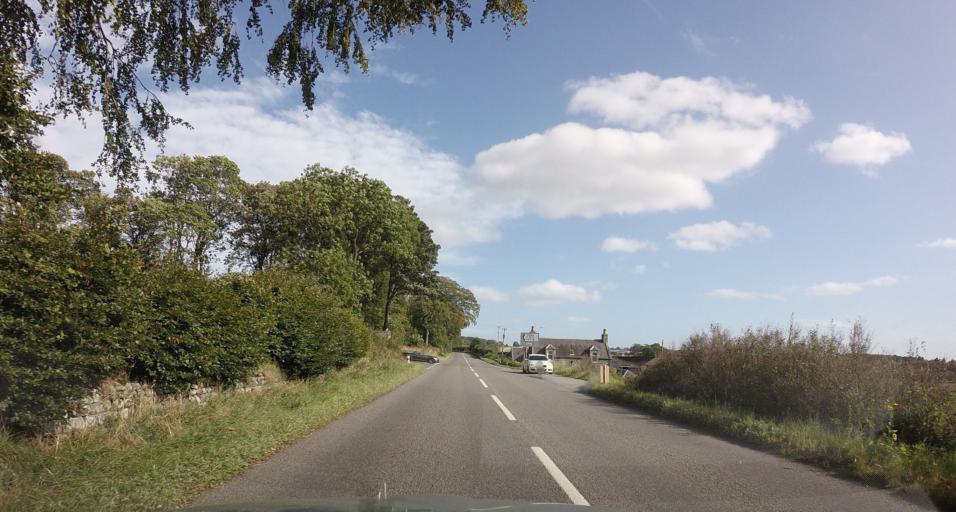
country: GB
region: Scotland
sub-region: Aberdeenshire
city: Westhill
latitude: 57.1560
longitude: -2.3306
